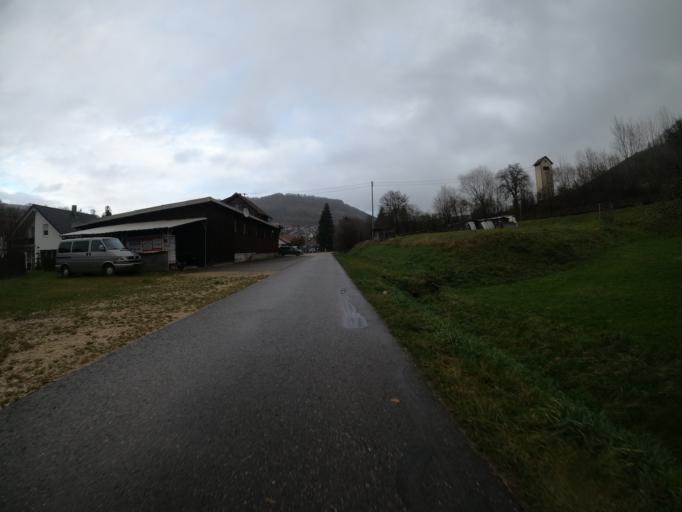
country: DE
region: Baden-Wuerttemberg
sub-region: Regierungsbezirk Stuttgart
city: Donzdorf
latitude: 48.7078
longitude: 9.8574
